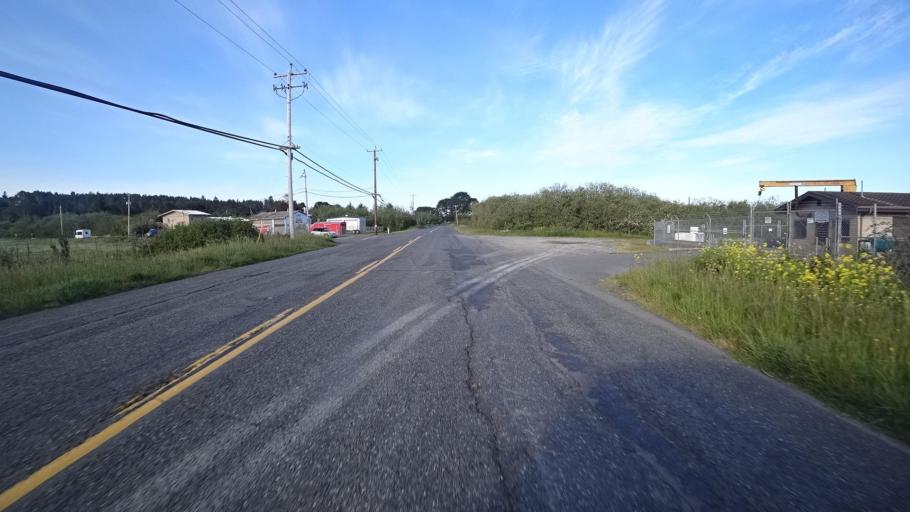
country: US
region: California
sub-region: Humboldt County
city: Humboldt Hill
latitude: 40.7378
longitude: -124.2066
